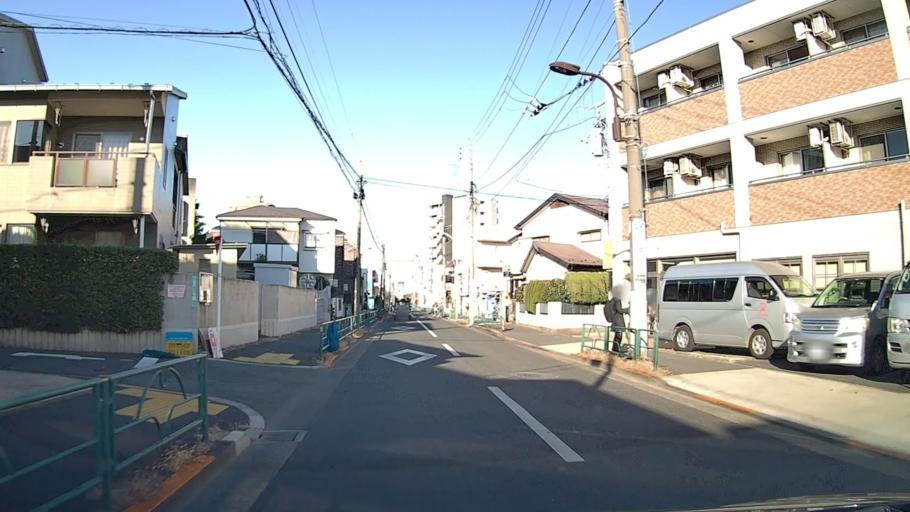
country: JP
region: Tokyo
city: Tokyo
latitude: 35.7275
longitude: 139.6767
